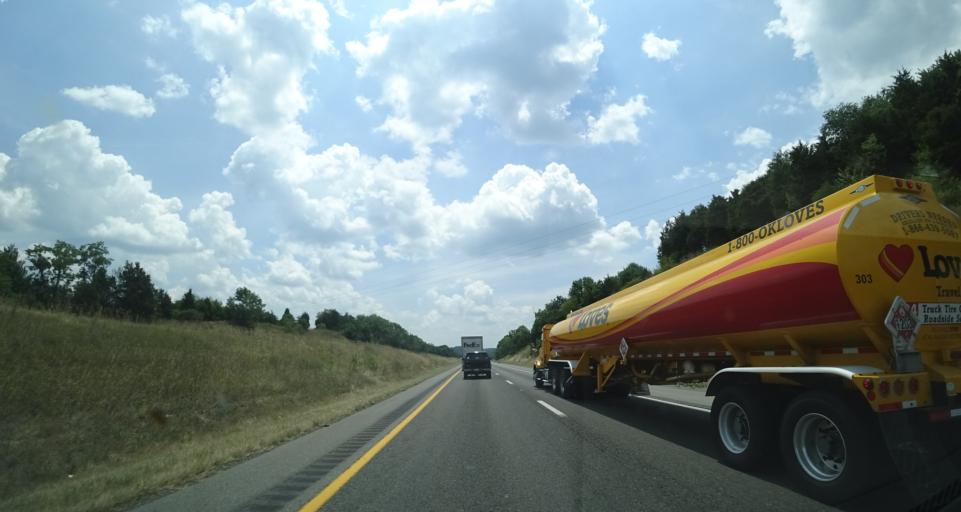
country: US
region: Virginia
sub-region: Pulaski County
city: Dublin
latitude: 37.0655
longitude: -80.7073
